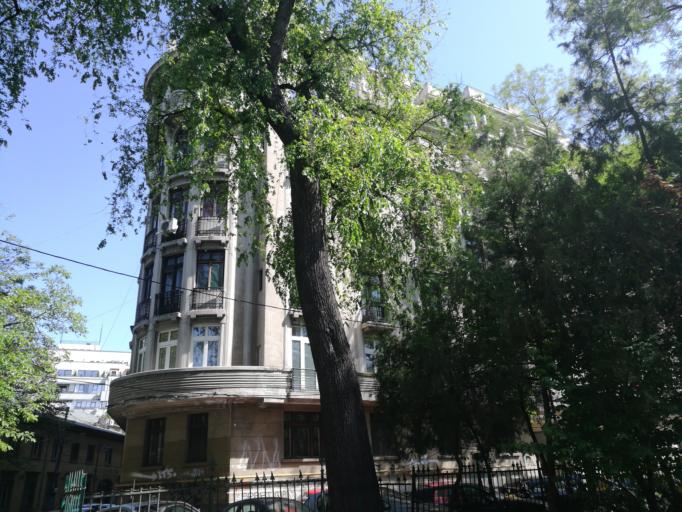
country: RO
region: Bucuresti
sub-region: Municipiul Bucuresti
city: Bucuresti
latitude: 44.4351
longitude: 26.0934
